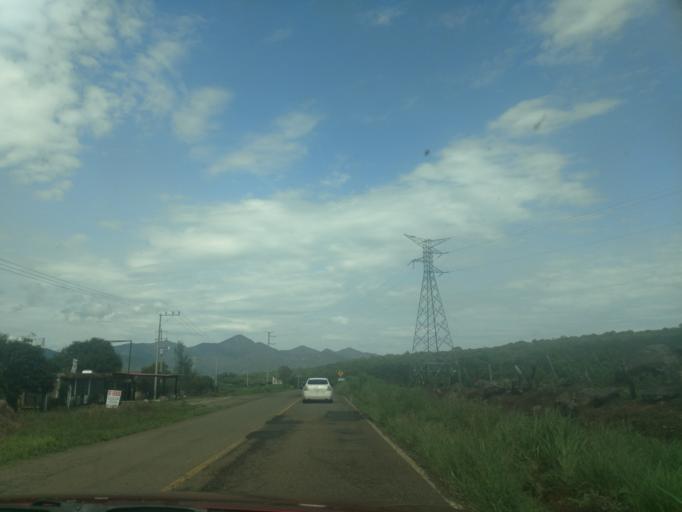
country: MX
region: Jalisco
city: Talpa de Allende
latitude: 20.4230
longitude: -104.7284
